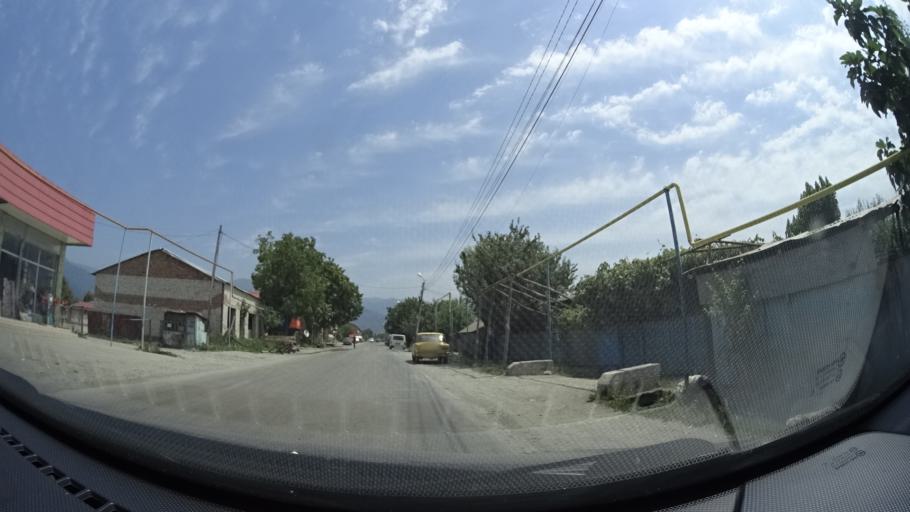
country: GE
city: Bagdadi
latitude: 41.8417
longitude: 46.1151
